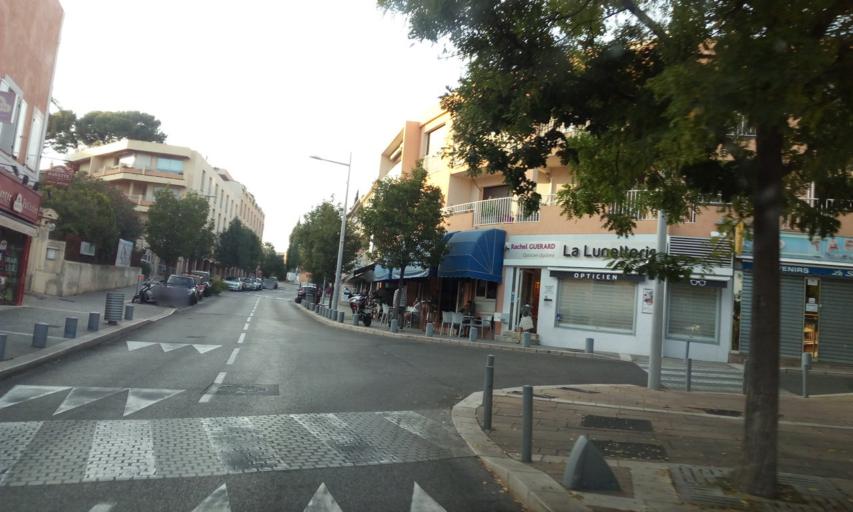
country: FR
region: Provence-Alpes-Cote d'Azur
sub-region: Departement du Var
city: Bandol
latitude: 43.1376
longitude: 5.7522
